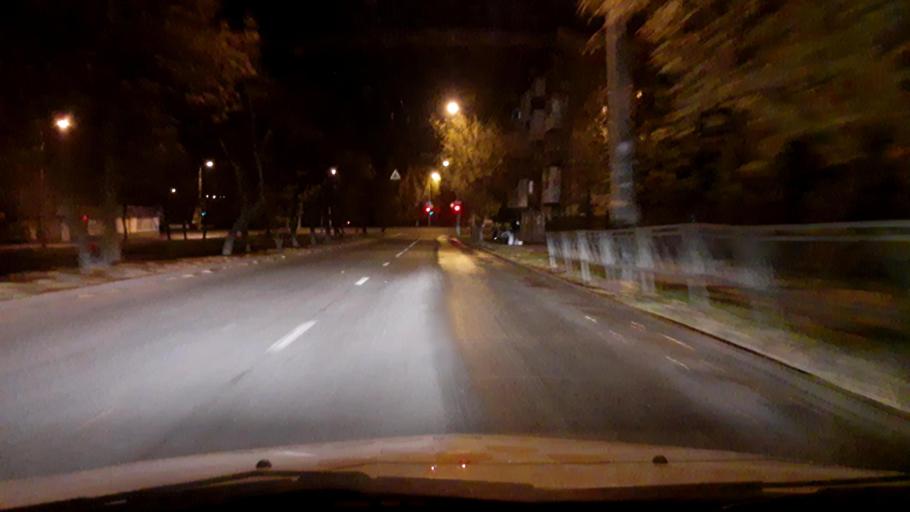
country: RU
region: Bashkortostan
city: Ufa
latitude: 54.8144
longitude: 56.1062
